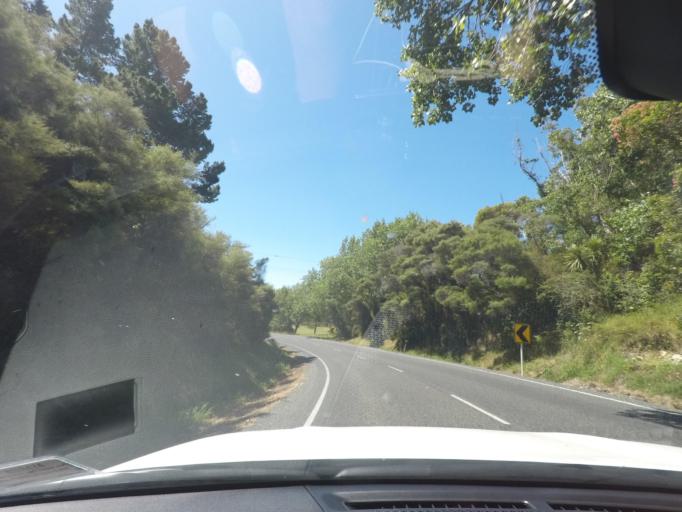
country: NZ
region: Auckland
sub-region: Auckland
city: Parakai
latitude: -36.5897
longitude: 174.3390
